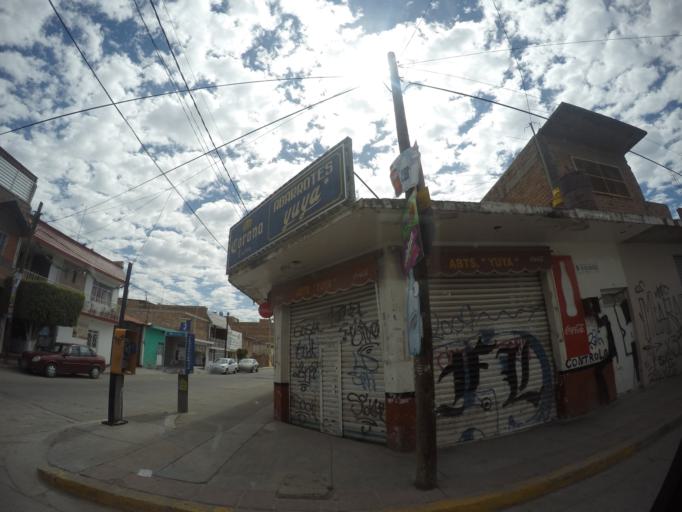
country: MX
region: Guanajuato
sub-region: Leon
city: San Jose de Duran (Los Troncoso)
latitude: 21.0927
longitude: -101.6808
